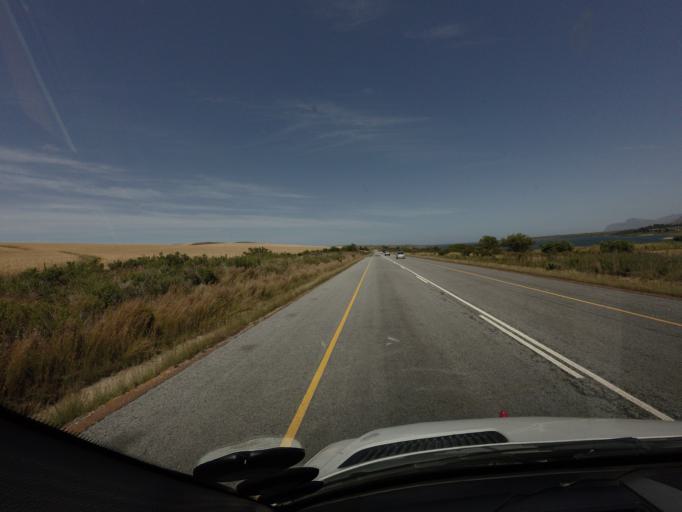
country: ZA
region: Western Cape
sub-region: Overberg District Municipality
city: Hermanus
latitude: -34.3195
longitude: 19.1472
